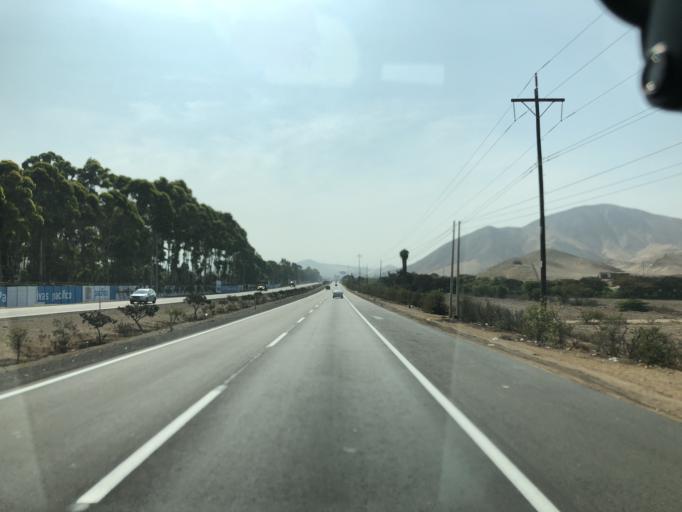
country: PE
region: Lima
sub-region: Provincia de Canete
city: Chilca
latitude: -12.5784
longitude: -76.6822
